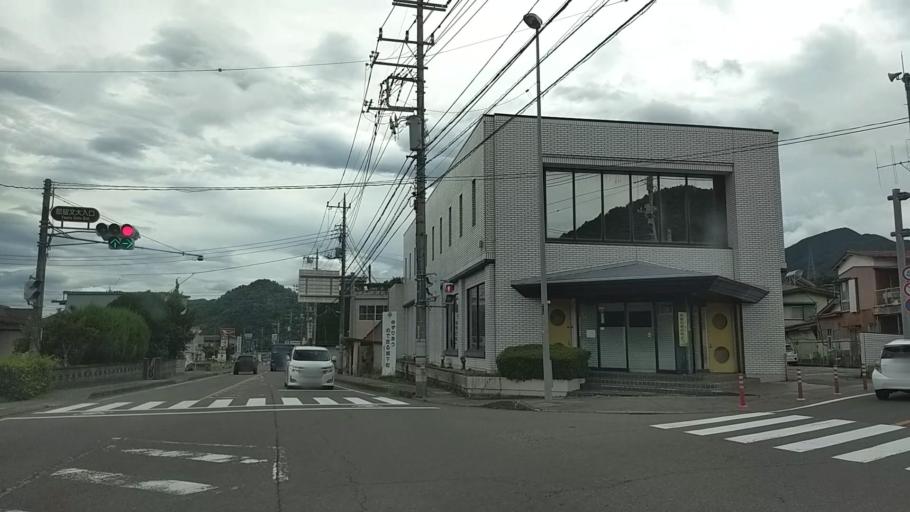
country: JP
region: Yamanashi
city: Otsuki
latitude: 35.5420
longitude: 138.8931
